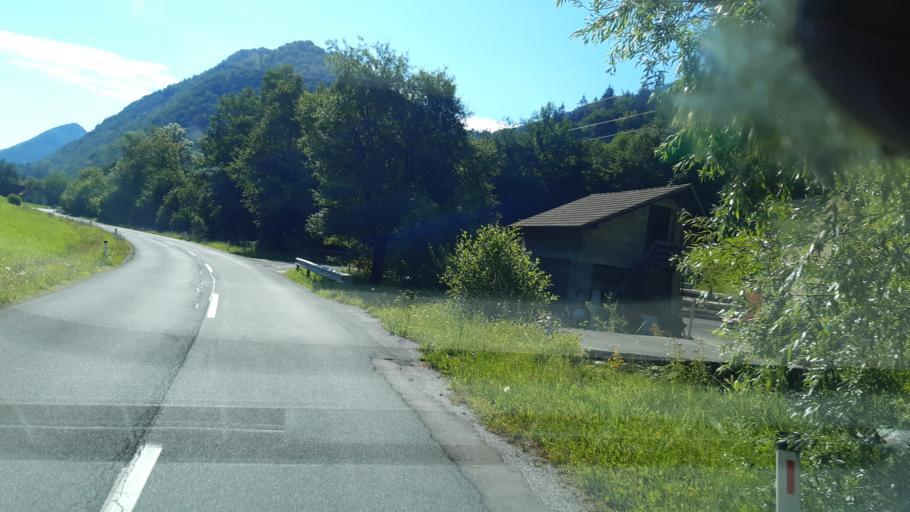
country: SI
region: Gornji Grad
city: Gornji Grad
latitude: 46.2139
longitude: 14.8552
